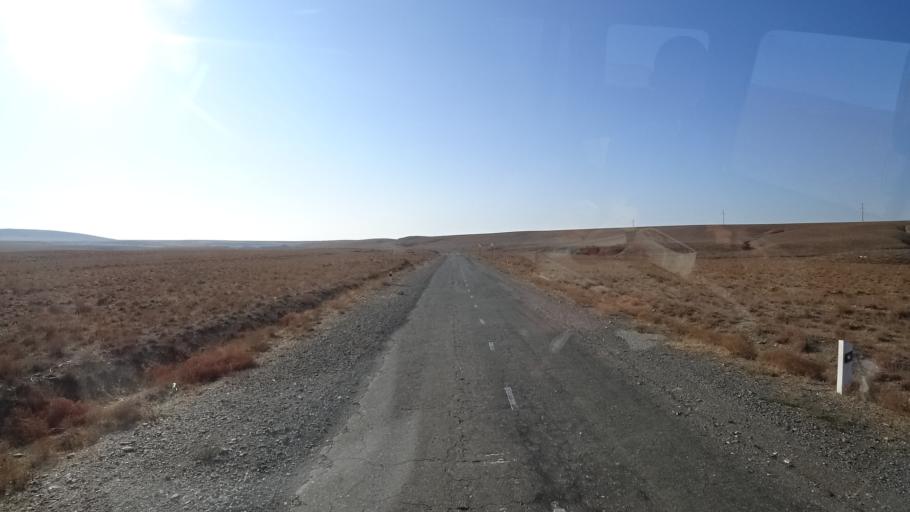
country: UZ
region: Navoiy
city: Beshrabot
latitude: 40.2602
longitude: 65.4845
